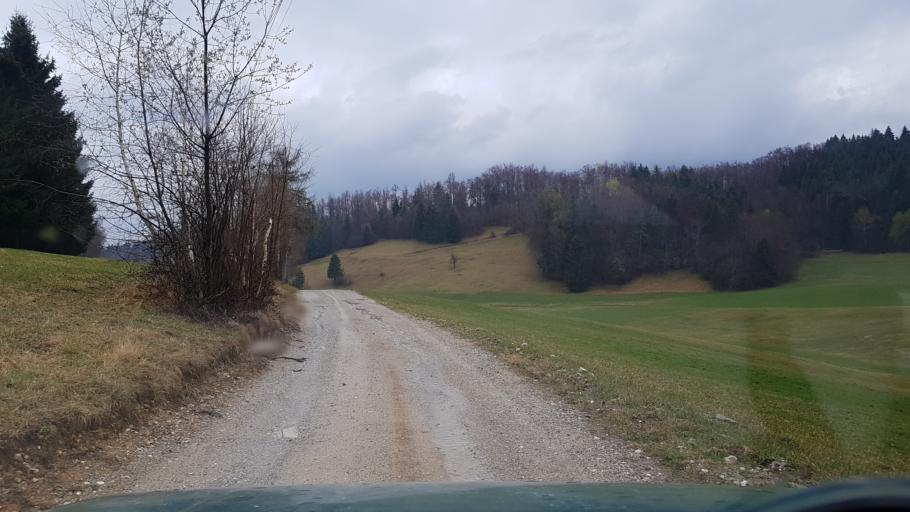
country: SI
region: Tolmin
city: Tolmin
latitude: 46.1379
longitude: 13.8462
